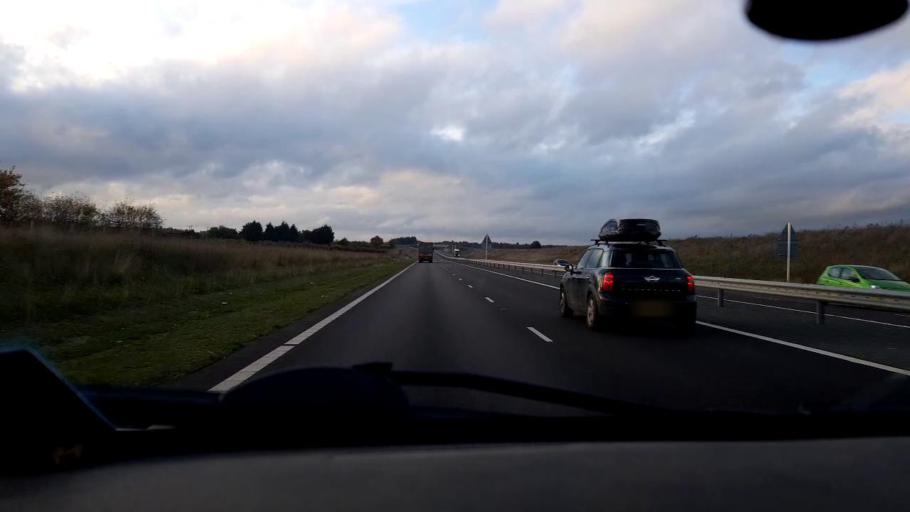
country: GB
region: England
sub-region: Norfolk
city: Horsford
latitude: 52.6887
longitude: 1.2357
